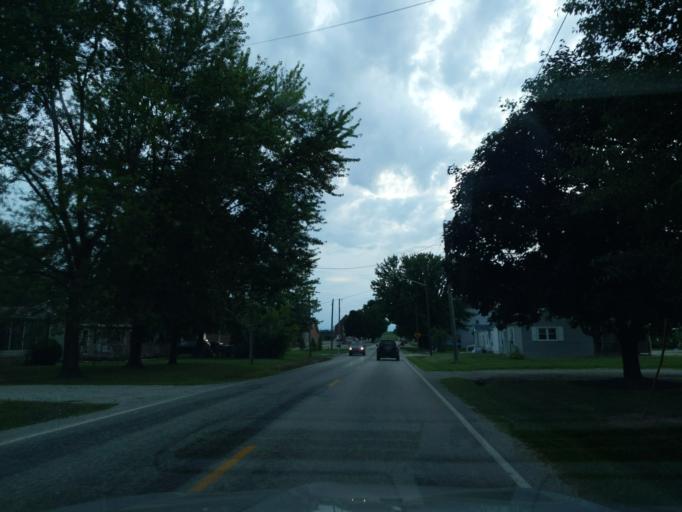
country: US
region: Indiana
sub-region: Ripley County
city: Osgood
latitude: 39.2050
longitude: -85.3256
